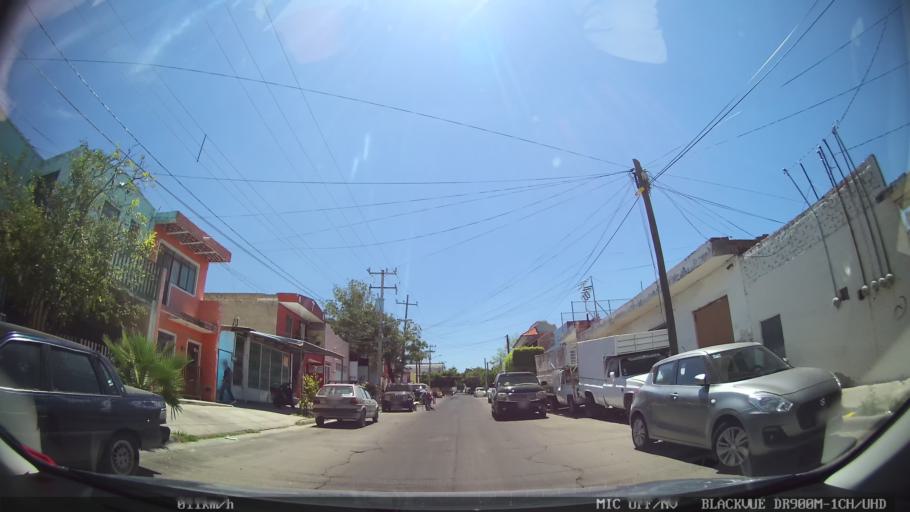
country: MX
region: Jalisco
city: Tlaquepaque
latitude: 20.6757
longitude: -103.2705
